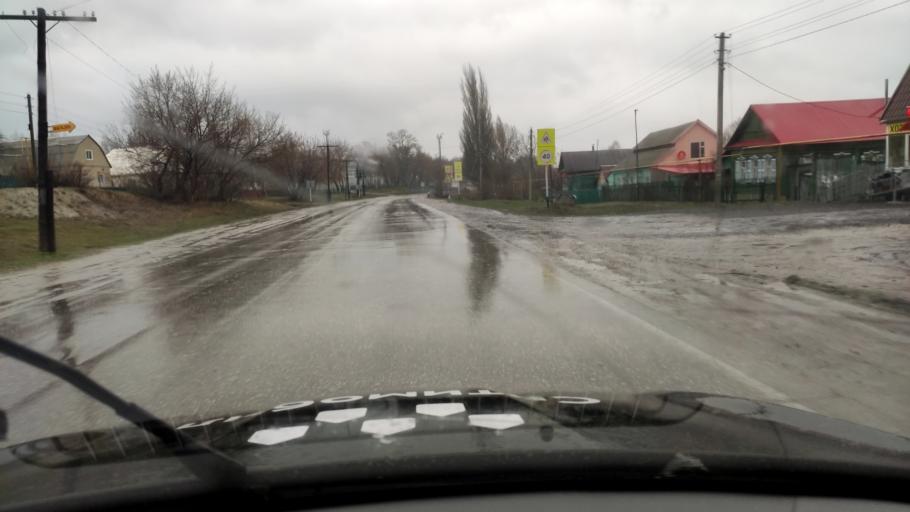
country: RU
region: Samara
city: Balasheyka
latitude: 53.2291
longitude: 48.2351
